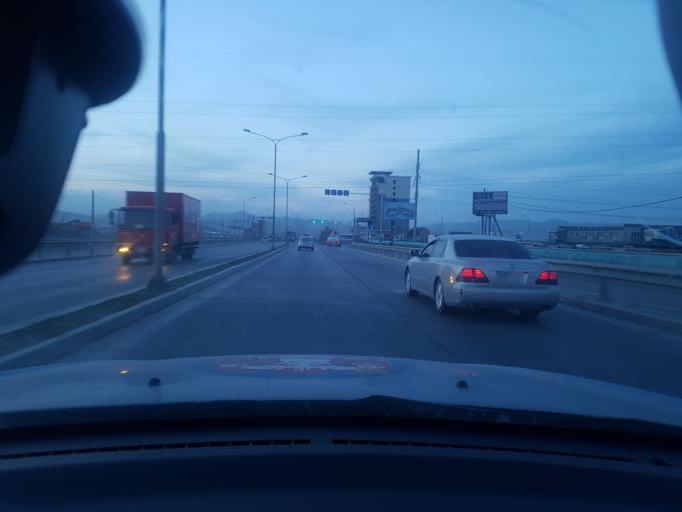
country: MN
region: Ulaanbaatar
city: Ulaanbaatar
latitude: 47.8890
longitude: 106.7853
